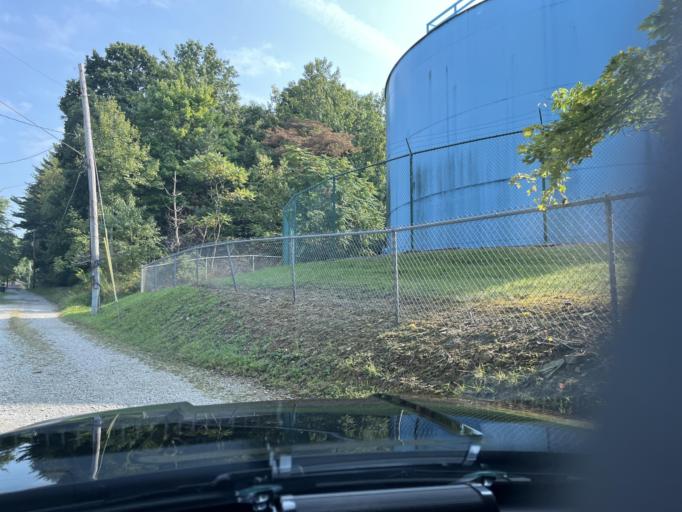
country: US
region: Pennsylvania
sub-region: Fayette County
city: Hopwood
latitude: 39.8516
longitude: -79.7073
